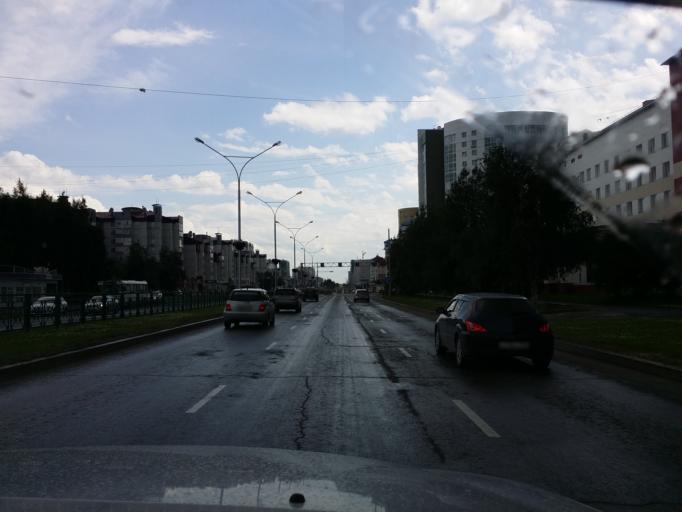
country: RU
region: Khanty-Mansiyskiy Avtonomnyy Okrug
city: Nizhnevartovsk
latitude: 60.9389
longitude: 76.5731
